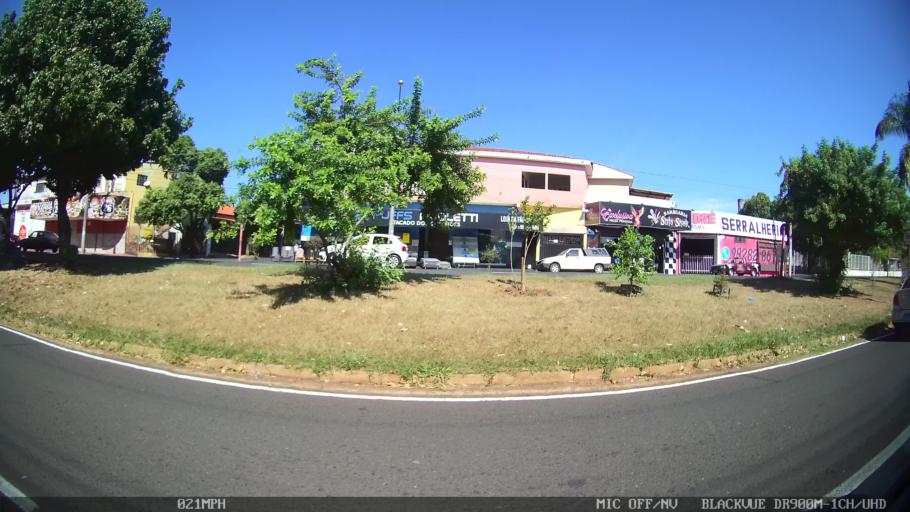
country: BR
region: Sao Paulo
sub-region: Sao Jose Do Rio Preto
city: Sao Jose do Rio Preto
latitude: -20.7755
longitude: -49.4111
